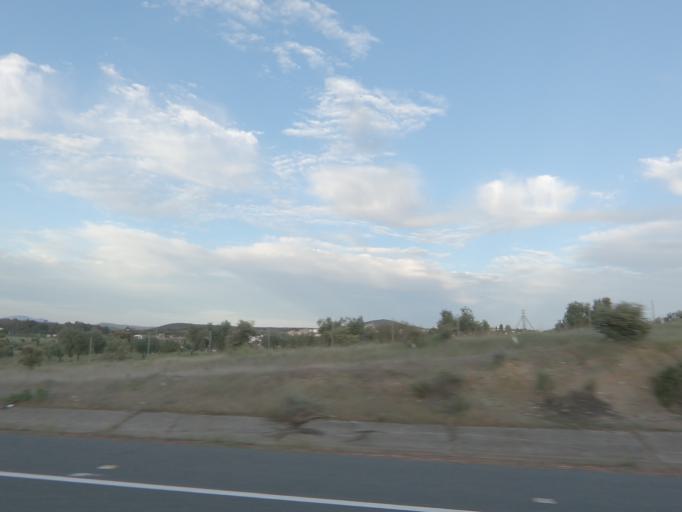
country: ES
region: Extremadura
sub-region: Provincia de Badajoz
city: Aljucen
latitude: 39.0438
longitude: -6.3388
